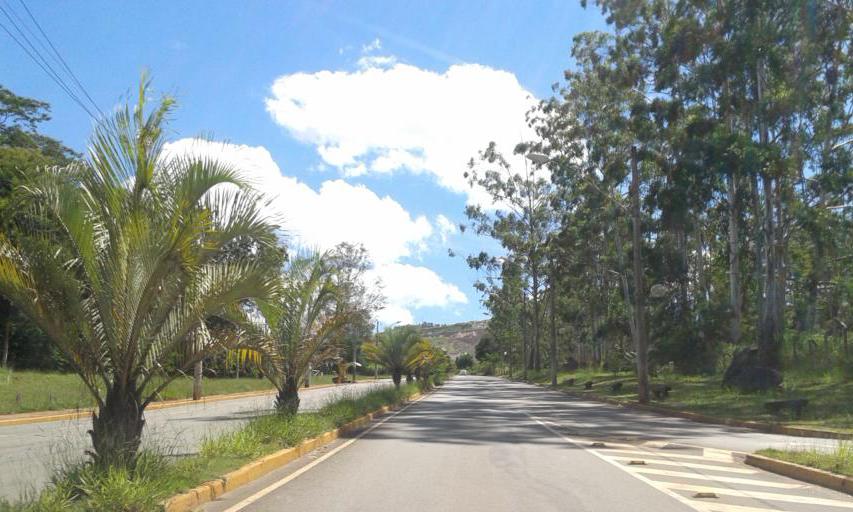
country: BR
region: Minas Gerais
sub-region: Itabira
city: Itabira
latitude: -19.6351
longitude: -43.2392
